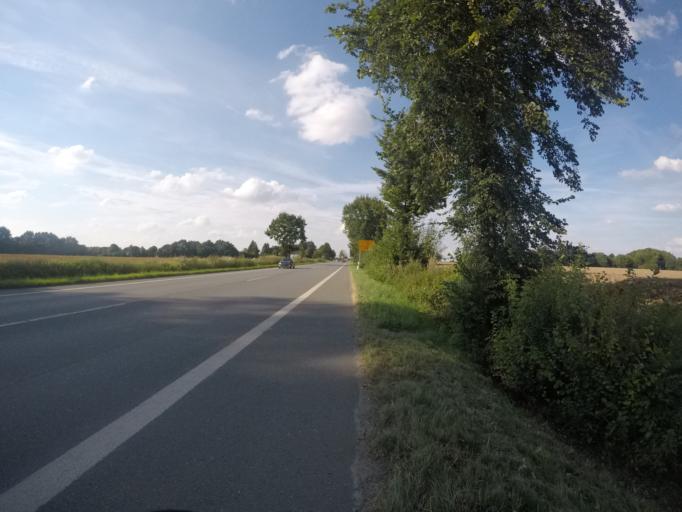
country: DE
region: North Rhine-Westphalia
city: Enger
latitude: 52.0887
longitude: 8.5860
